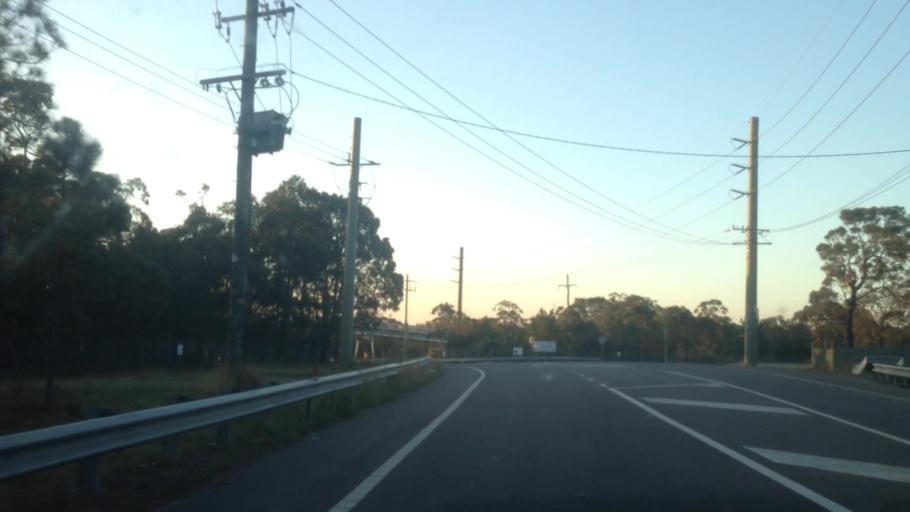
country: AU
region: New South Wales
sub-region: Wyong Shire
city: Kingfisher Shores
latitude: -33.1740
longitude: 151.5395
